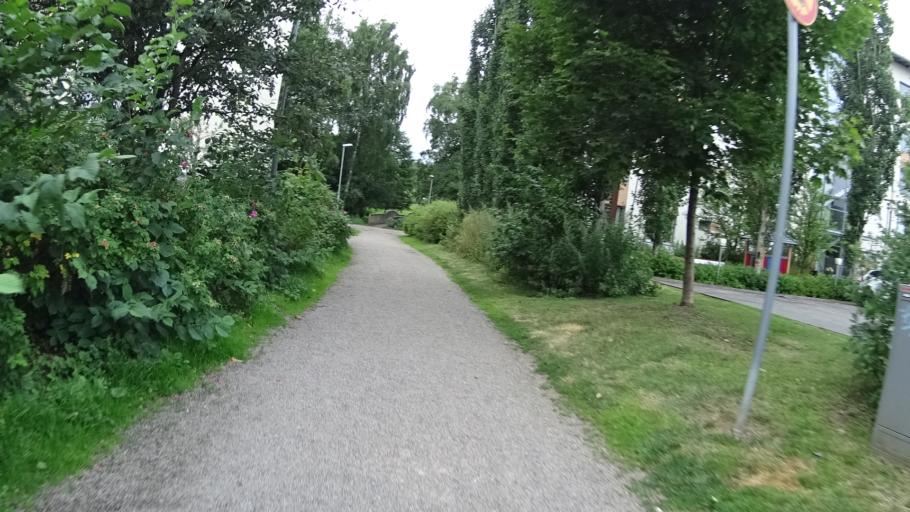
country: FI
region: Uusimaa
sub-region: Helsinki
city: Teekkarikylae
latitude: 60.2166
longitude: 24.8644
